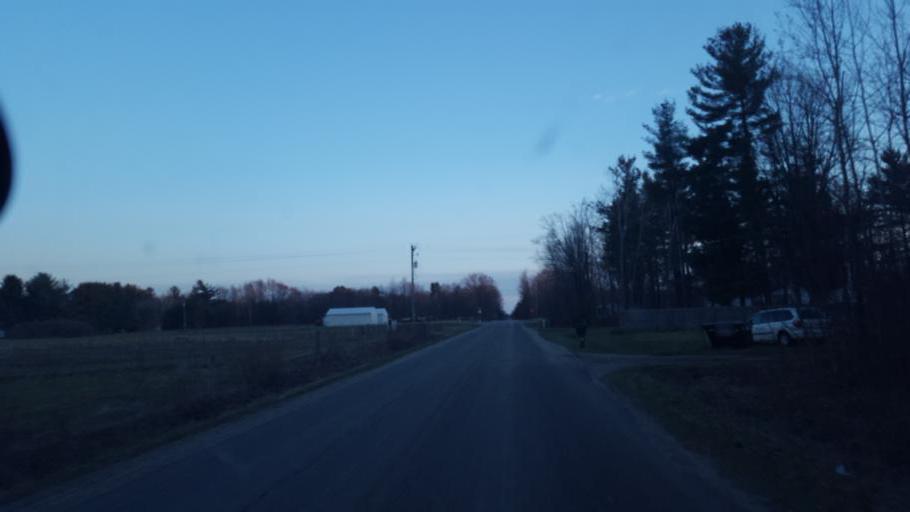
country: US
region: Michigan
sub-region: Montcalm County
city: Howard City
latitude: 43.5272
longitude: -85.4824
